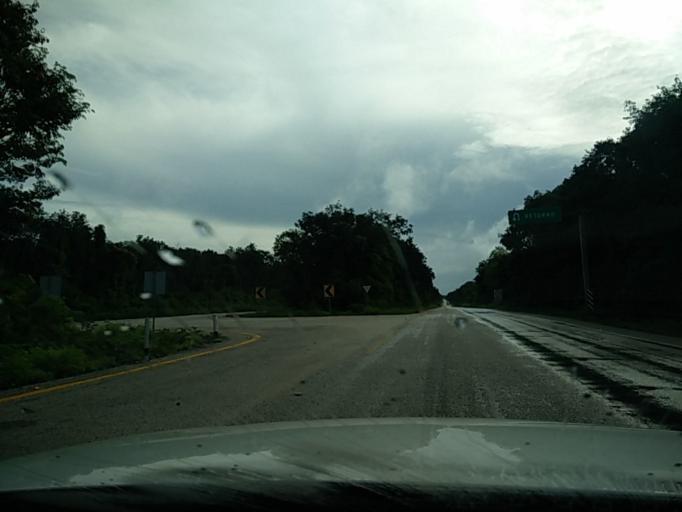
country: MX
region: Yucatan
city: Tunkas
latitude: 20.7547
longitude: -88.7427
